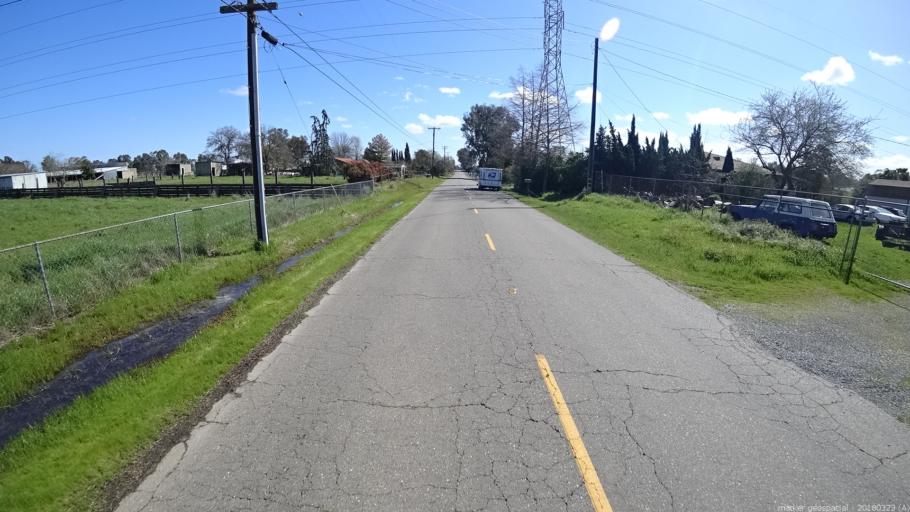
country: US
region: California
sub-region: Sacramento County
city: Rio Linda
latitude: 38.6800
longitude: -121.4270
